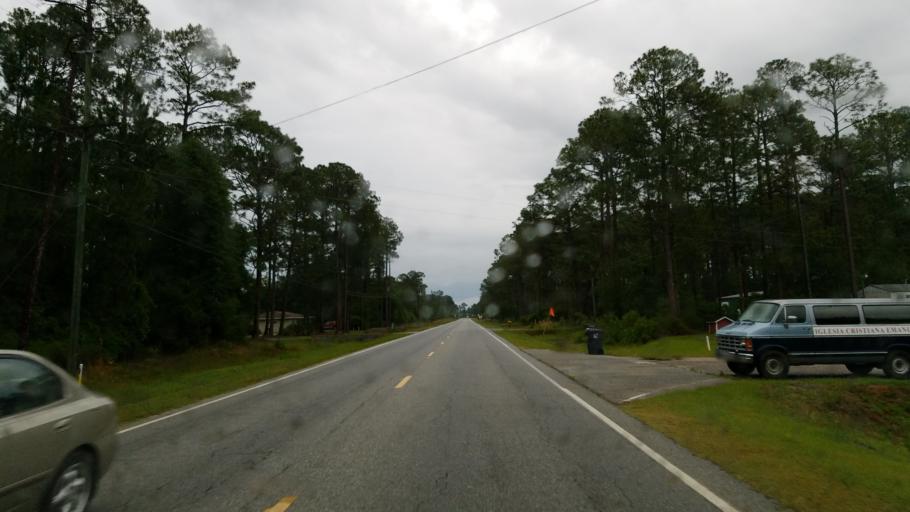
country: US
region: Georgia
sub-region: Lanier County
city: Lakeland
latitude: 31.0454
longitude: -83.1078
